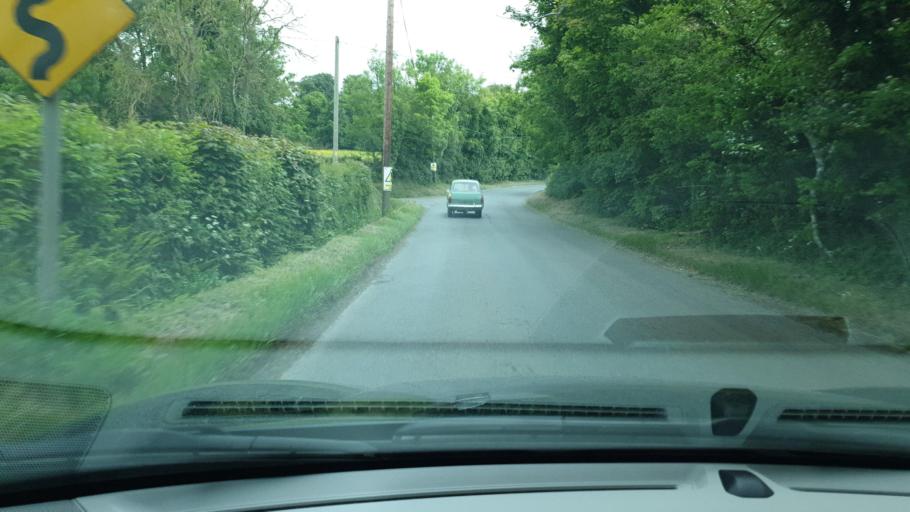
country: IE
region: Leinster
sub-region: An Mhi
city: Ashbourne
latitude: 53.5457
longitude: -6.4107
